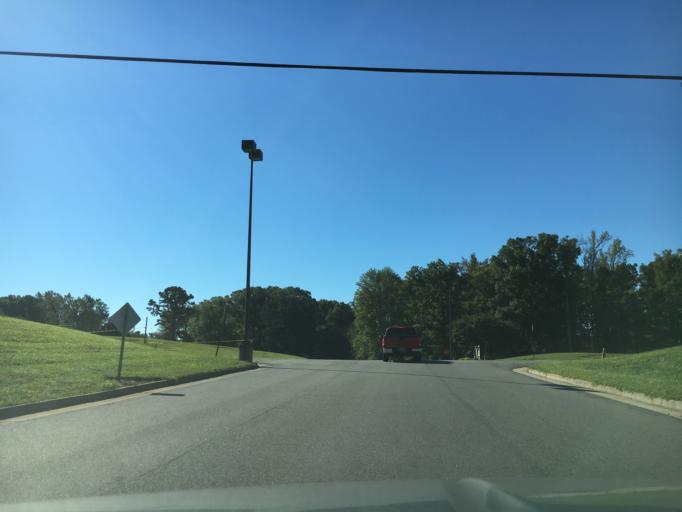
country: US
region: Virginia
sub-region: Goochland County
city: Goochland
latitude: 37.6991
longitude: -77.8870
